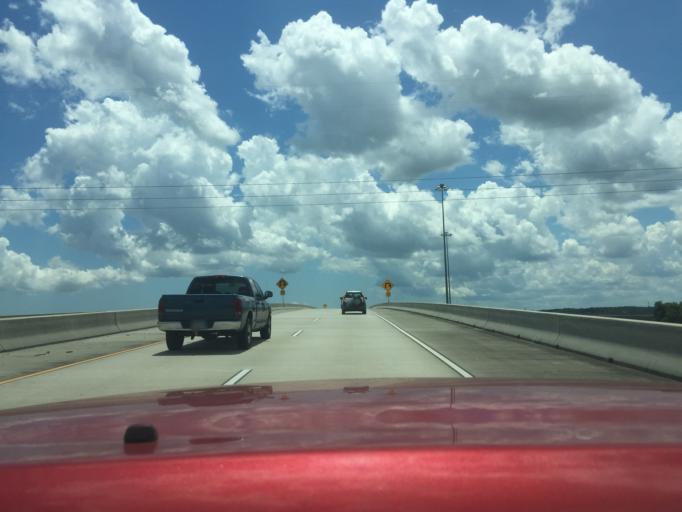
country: US
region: Georgia
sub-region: Chatham County
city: Georgetown
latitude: 31.9857
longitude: -81.1999
